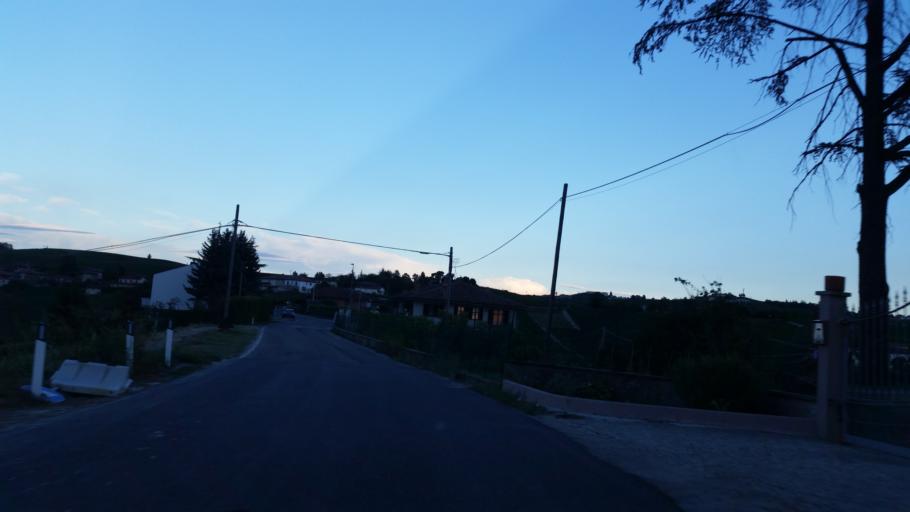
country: IT
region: Piedmont
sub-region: Provincia di Cuneo
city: Barbaresco
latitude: 44.7142
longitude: 8.0858
